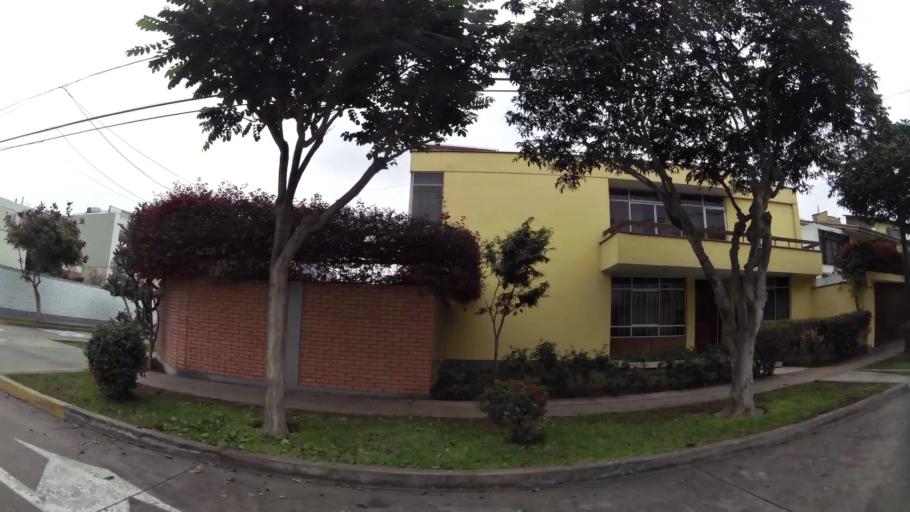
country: PE
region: Lima
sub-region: Lima
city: San Luis
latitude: -12.0964
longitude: -77.0145
